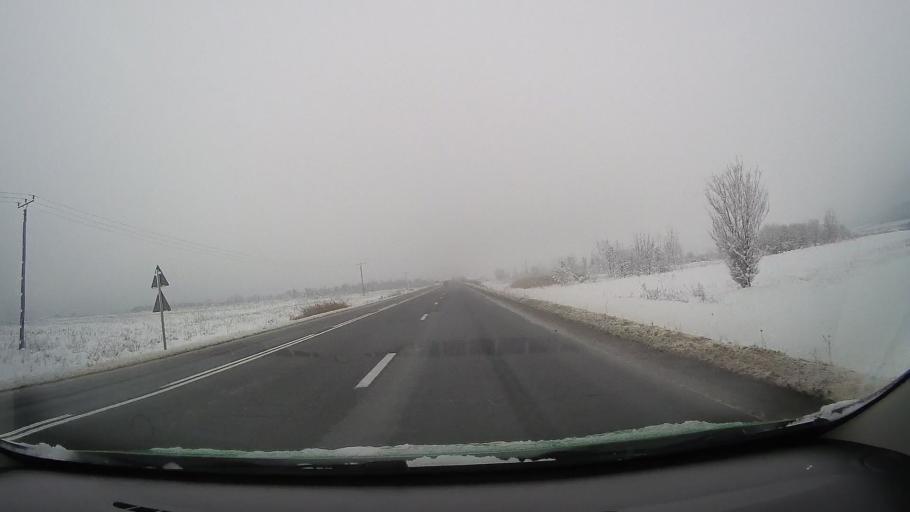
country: RO
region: Sibiu
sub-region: Oras Saliste
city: Saliste
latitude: 45.7893
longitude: 23.9261
